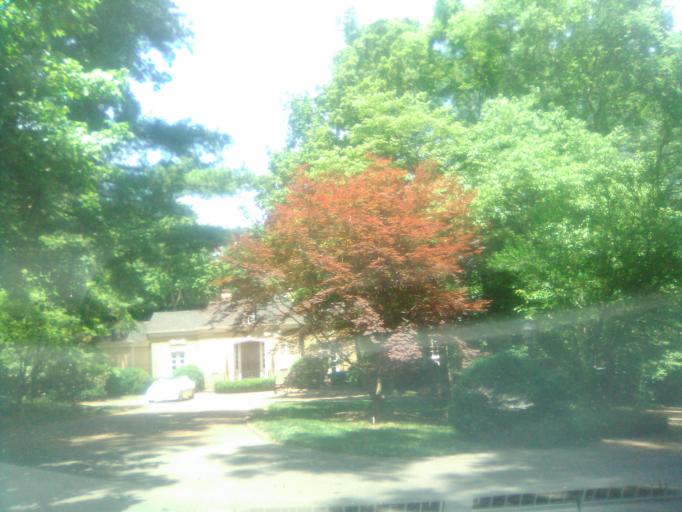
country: US
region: Tennessee
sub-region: Davidson County
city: Belle Meade
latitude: 36.1170
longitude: -86.8455
